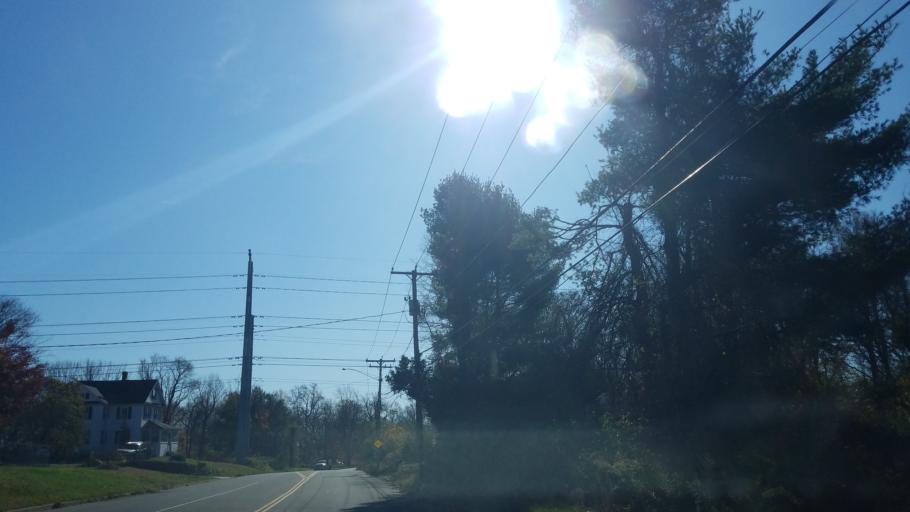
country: US
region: Connecticut
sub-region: New Haven County
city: City of Milford (balance)
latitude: 41.2451
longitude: -73.0747
